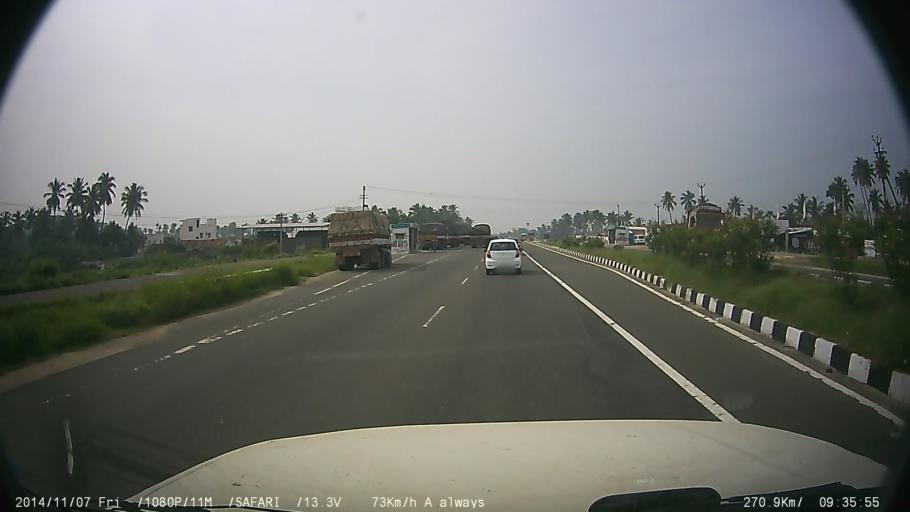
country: IN
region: Tamil Nadu
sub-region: Erode
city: Bhavani
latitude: 11.3719
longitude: 77.6492
